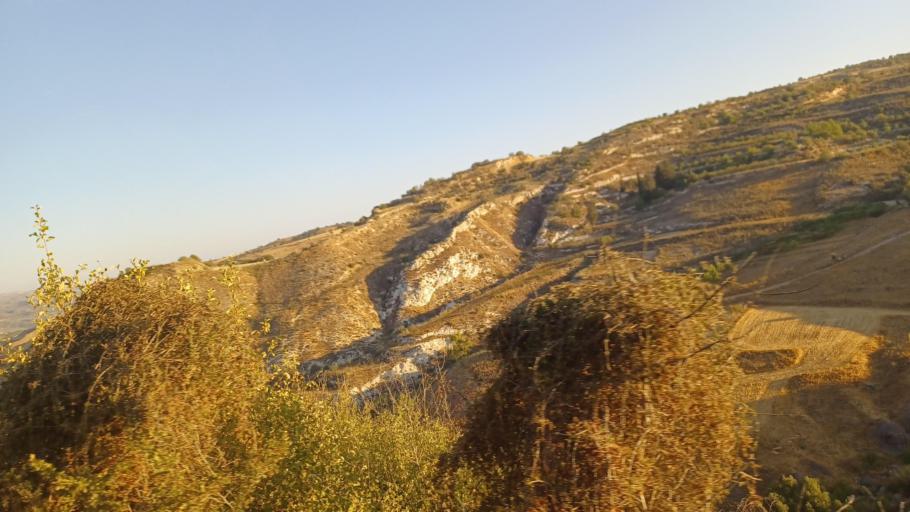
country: CY
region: Pafos
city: Tala
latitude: 34.9058
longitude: 32.5173
